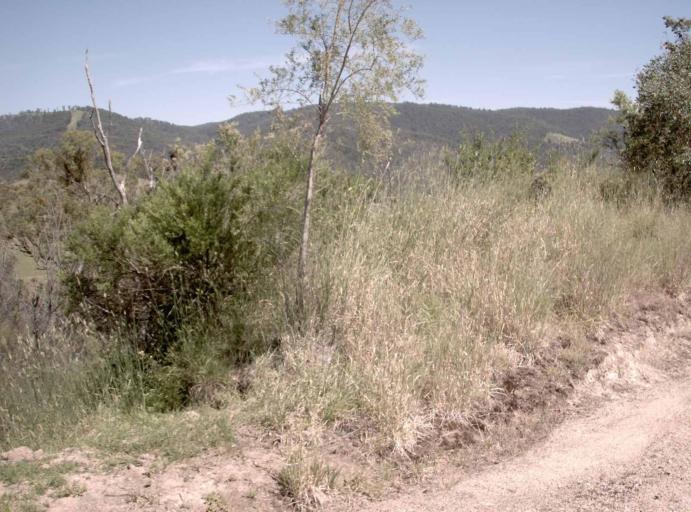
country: AU
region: Victoria
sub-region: East Gippsland
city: Lakes Entrance
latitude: -37.4902
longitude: 148.1862
